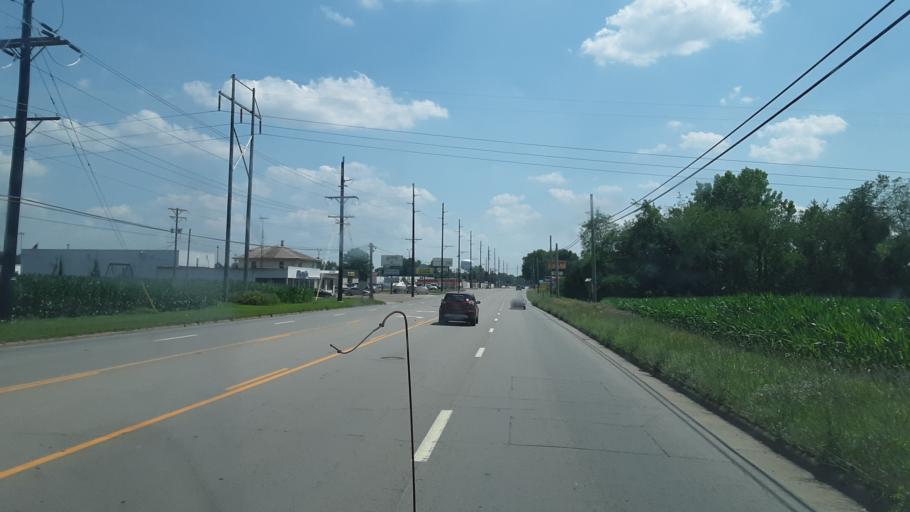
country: US
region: Ohio
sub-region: Stark County
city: Navarre
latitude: 40.7444
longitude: -81.5170
